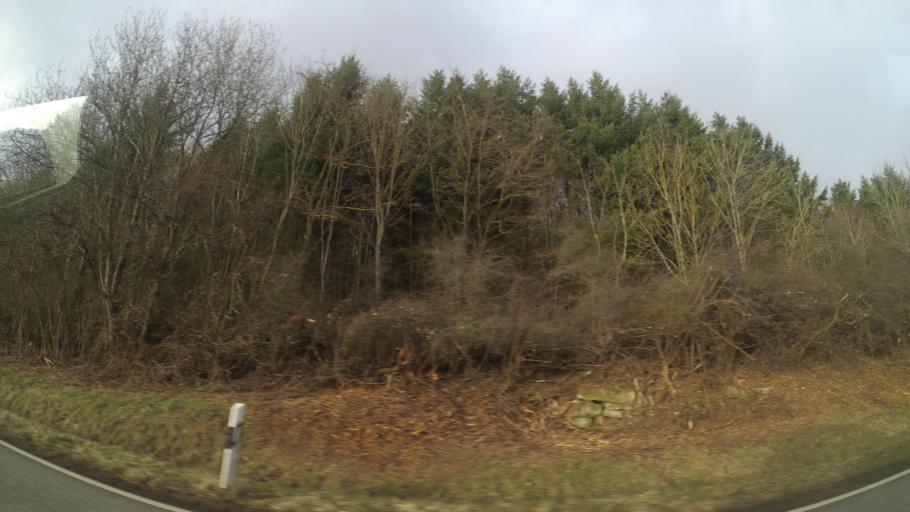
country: DE
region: Rheinland-Pfalz
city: Ulmet
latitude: 49.5810
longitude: 7.4378
